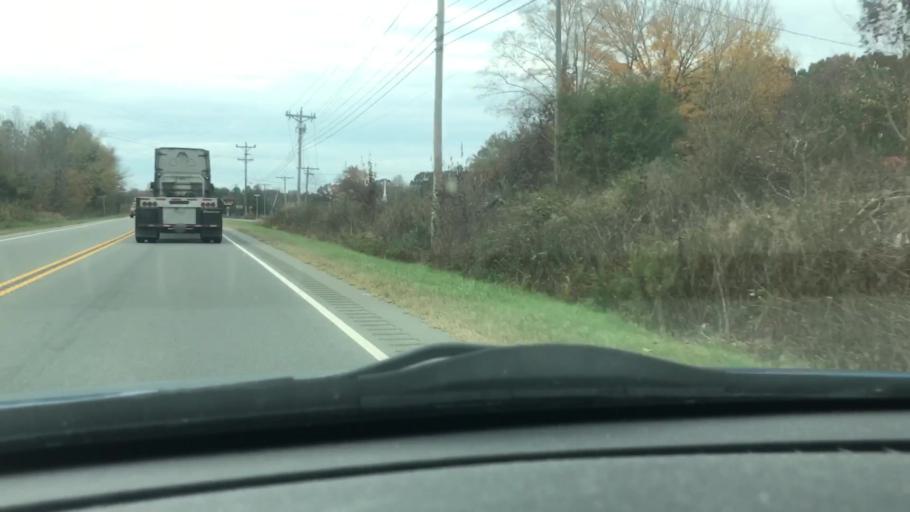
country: US
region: North Carolina
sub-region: Davidson County
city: Lexington
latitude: 35.8012
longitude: -80.1570
